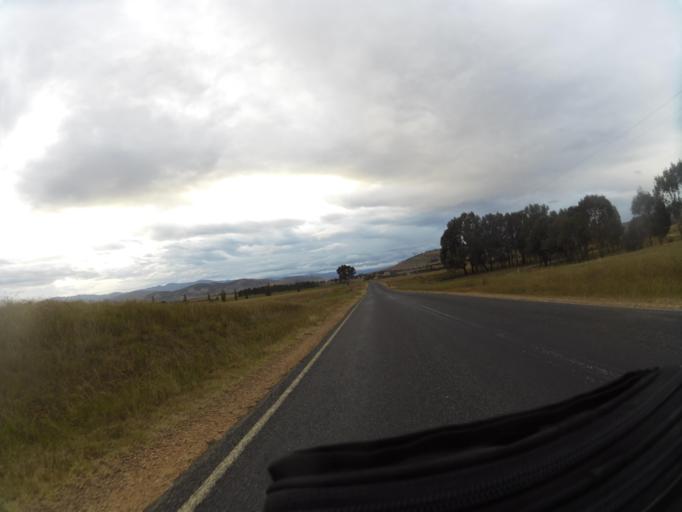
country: AU
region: New South Wales
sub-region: Greater Hume Shire
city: Holbrook
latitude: -36.0597
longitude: 147.9444
